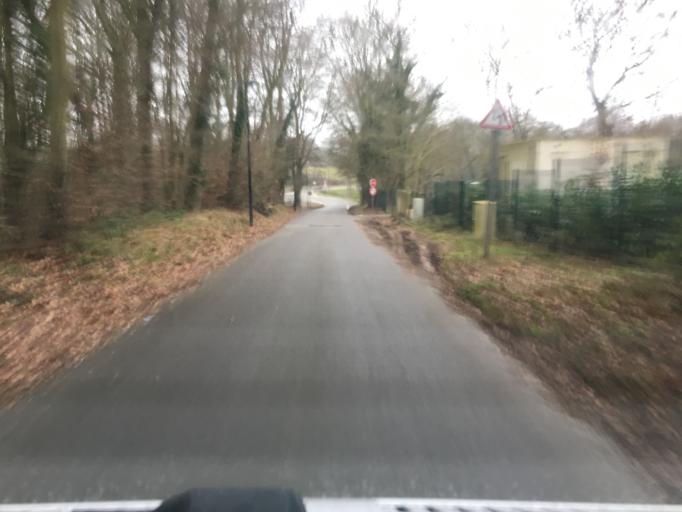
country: FR
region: Picardie
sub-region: Departement de la Somme
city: Saint-Valery-sur-Somme
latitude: 50.1770
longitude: 1.6369
